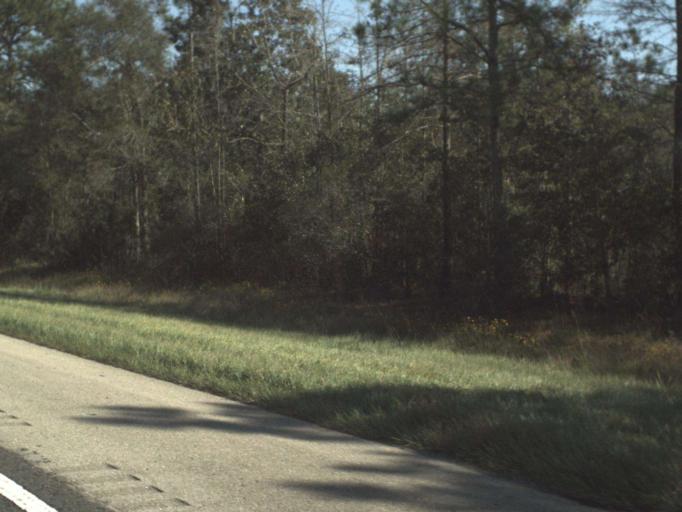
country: US
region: Florida
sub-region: Washington County
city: Chipley
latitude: 30.7461
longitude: -85.5043
